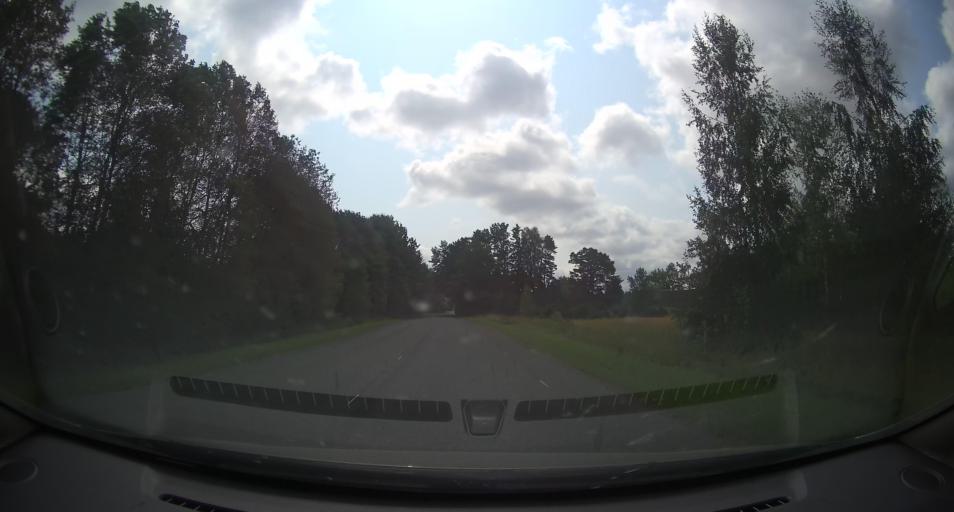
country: EE
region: Paernumaa
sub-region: Audru vald
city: Audru
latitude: 58.4936
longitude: 24.3357
